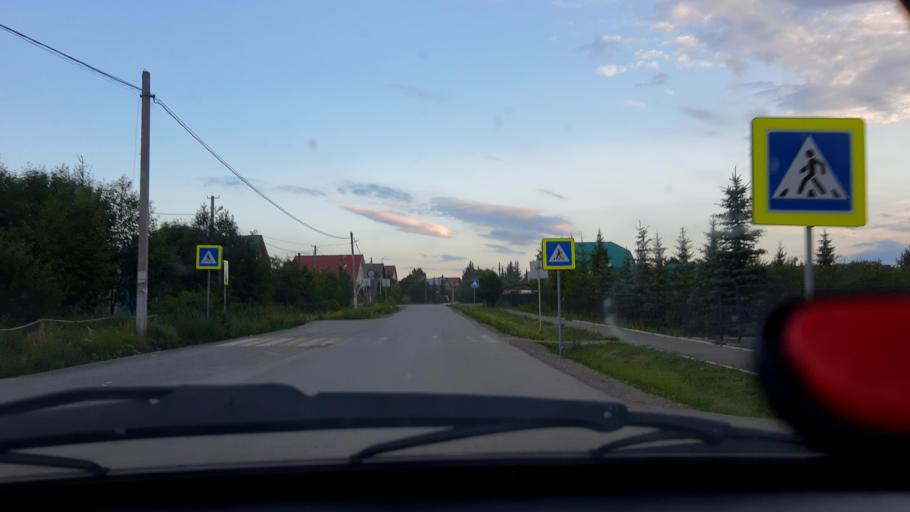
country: RU
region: Bashkortostan
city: Avdon
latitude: 54.4936
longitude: 55.8979
